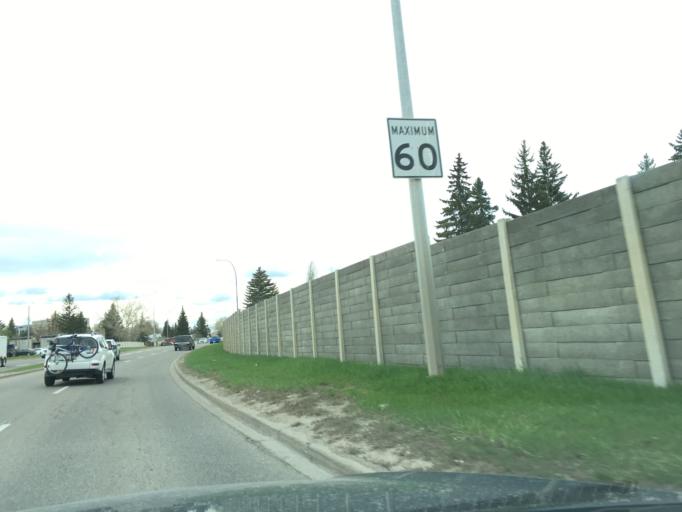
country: CA
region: Alberta
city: Calgary
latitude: 50.9642
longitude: -114.0597
